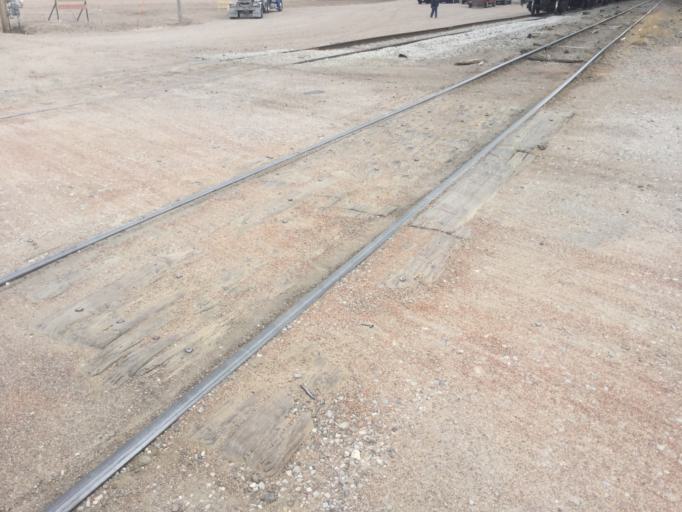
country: US
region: Kansas
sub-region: Haskell County
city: Sublette
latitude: 37.4813
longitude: -100.8529
